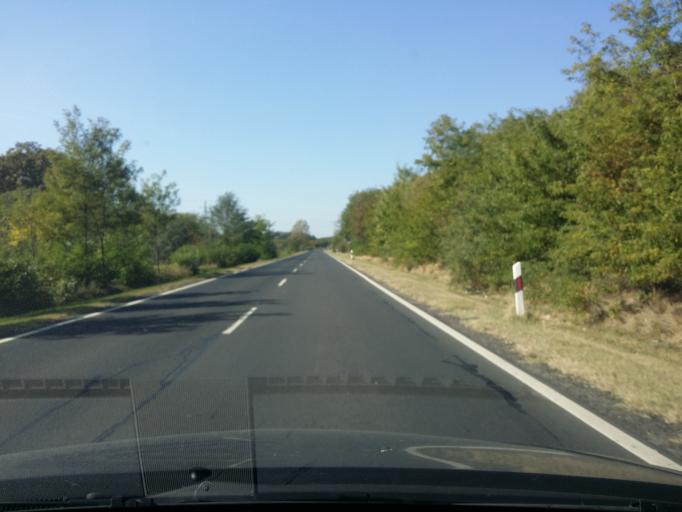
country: HU
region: Bacs-Kiskun
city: Nyarlorinc
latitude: 46.8684
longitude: 19.8628
